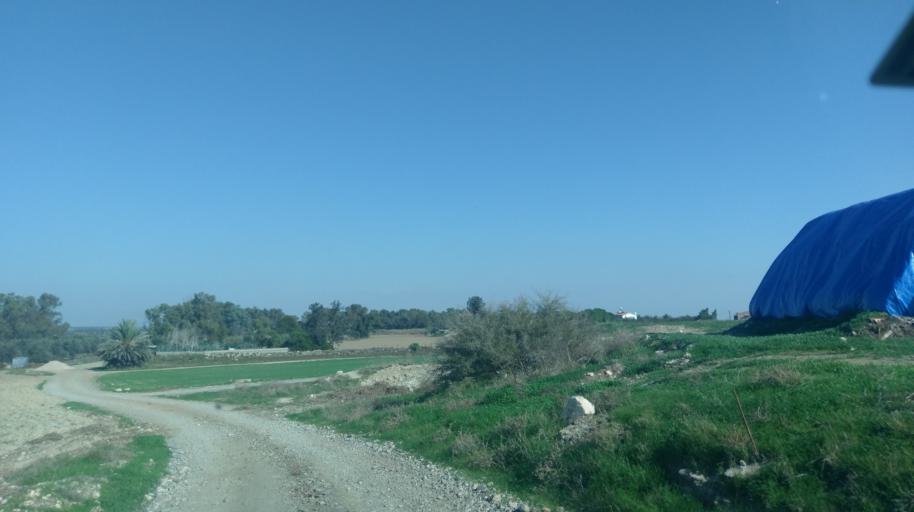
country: CY
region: Larnaka
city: Athienou
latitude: 35.1768
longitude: 33.5511
